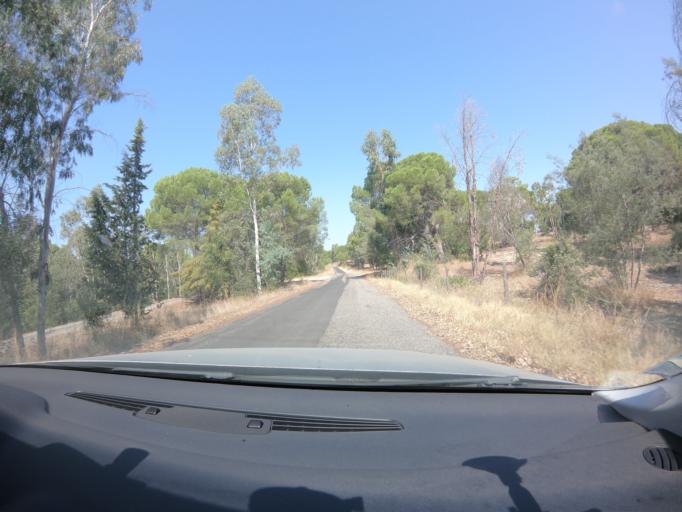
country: PT
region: Setubal
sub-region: Alcacer do Sal
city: Alcacer do Sal
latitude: 38.2509
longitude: -8.2975
